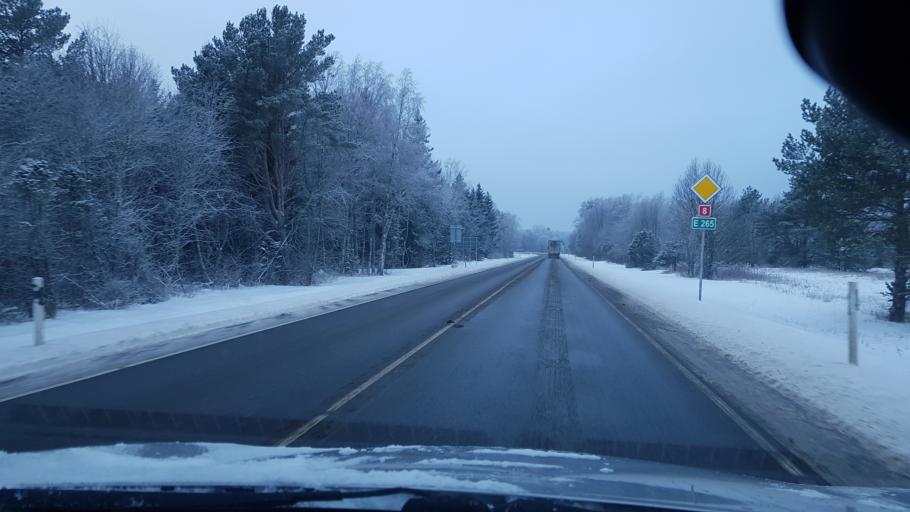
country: EE
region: Harju
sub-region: Paldiski linn
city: Paldiski
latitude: 59.3435
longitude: 24.1921
